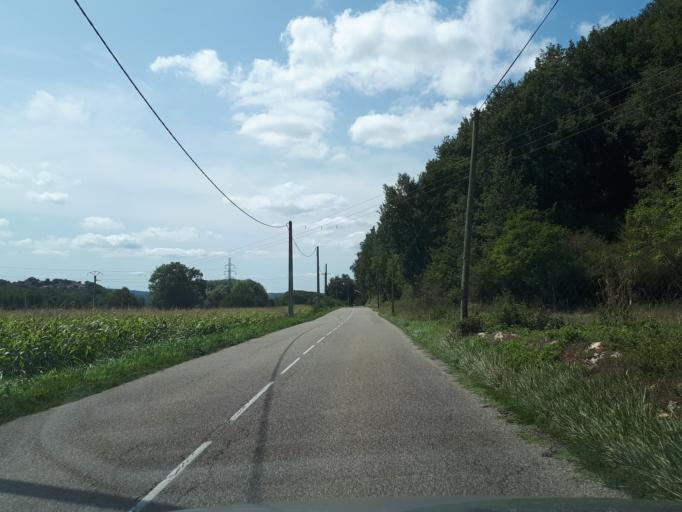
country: FR
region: Rhone-Alpes
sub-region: Departement de l'Isere
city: L'Isle-d'Abeau
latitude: 45.6348
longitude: 5.2230
